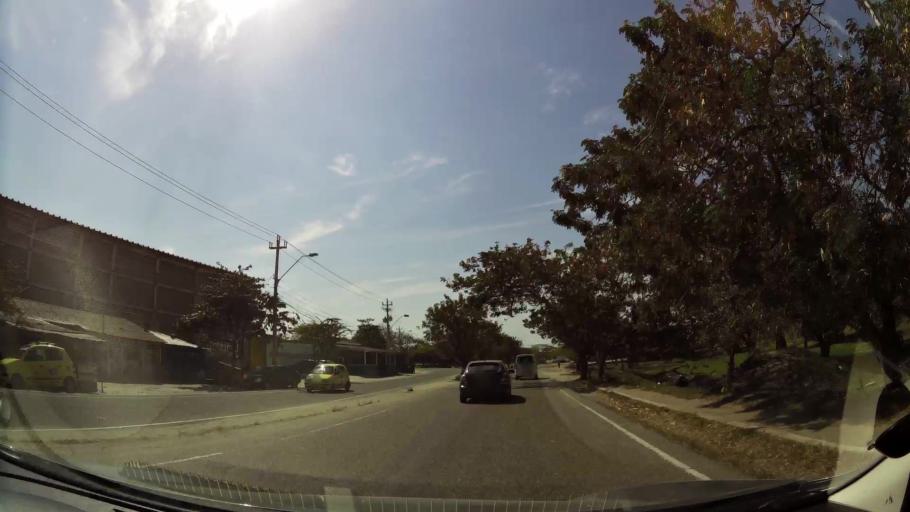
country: CO
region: Atlantico
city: Barranquilla
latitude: 10.9426
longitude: -74.8324
